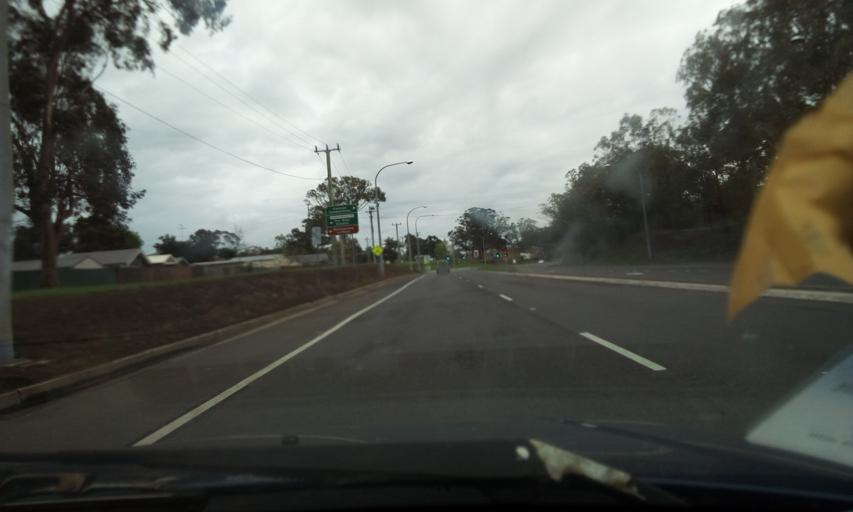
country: AU
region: New South Wales
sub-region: Camden
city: Camden South
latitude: -34.0780
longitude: 150.6948
